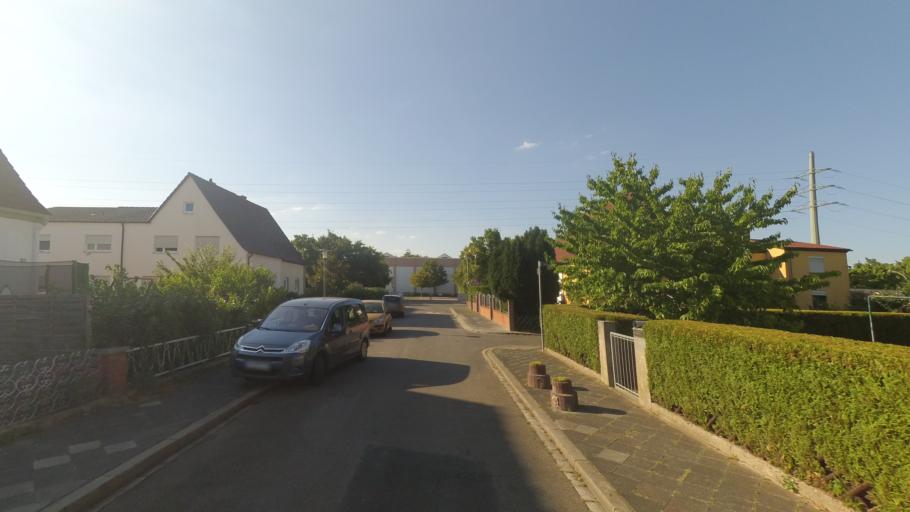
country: DE
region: Rheinland-Pfalz
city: Gartenstadt
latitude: 49.4673
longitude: 8.4043
